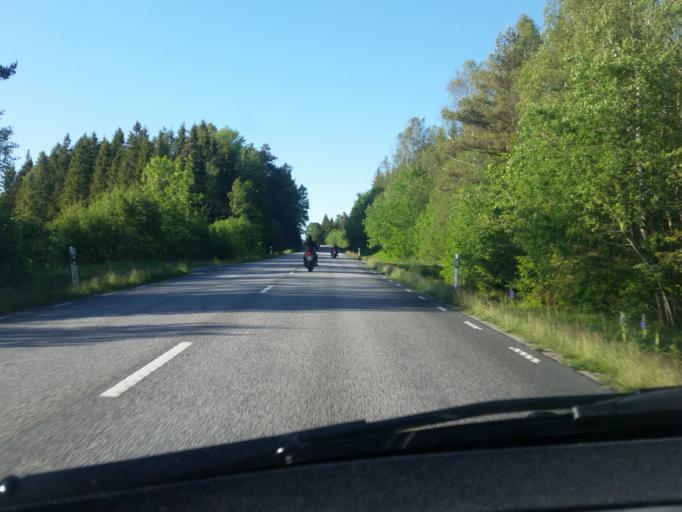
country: SE
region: Vaestra Goetaland
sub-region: Fargelanda Kommun
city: Faergelanda
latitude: 58.5312
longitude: 11.9814
